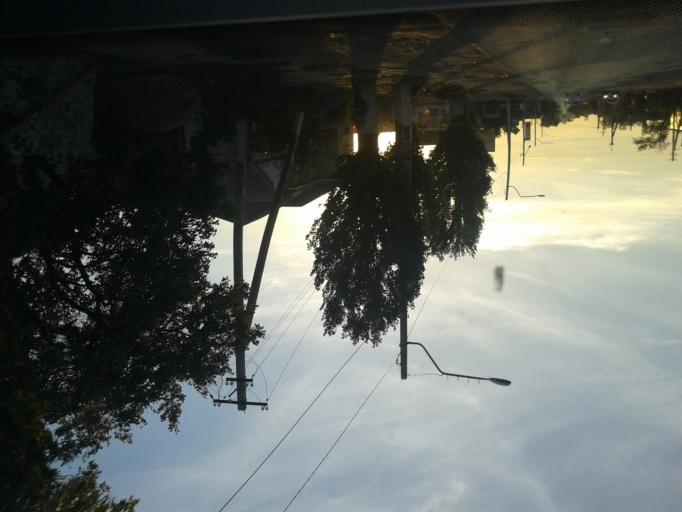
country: RU
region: Volgograd
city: Krasnoslobodsk
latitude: 48.7037
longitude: 44.5661
